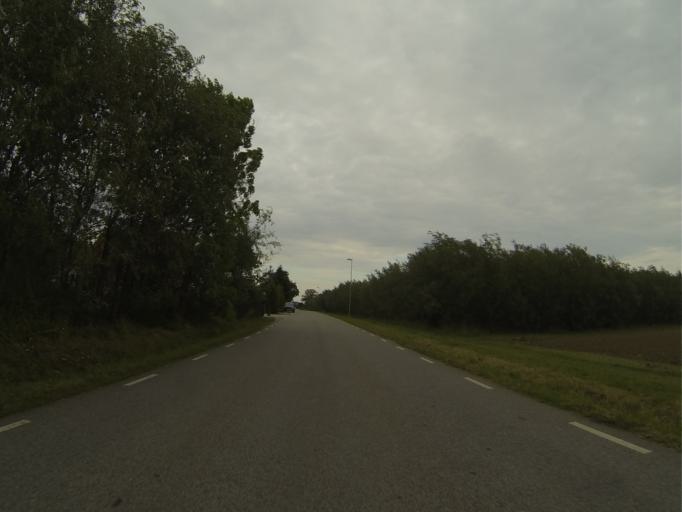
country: SE
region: Skane
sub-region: Staffanstorps Kommun
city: Hjaerup
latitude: 55.6394
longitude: 13.1456
